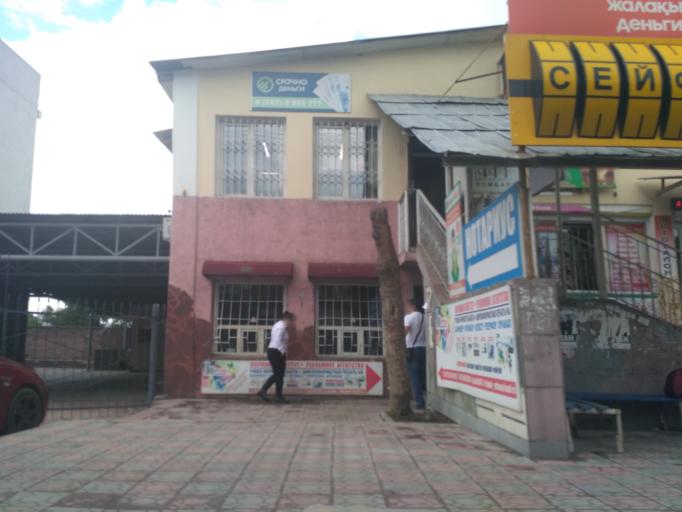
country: KZ
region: Almaty Oblysy
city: Burunday
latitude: 43.2016
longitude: 76.6268
